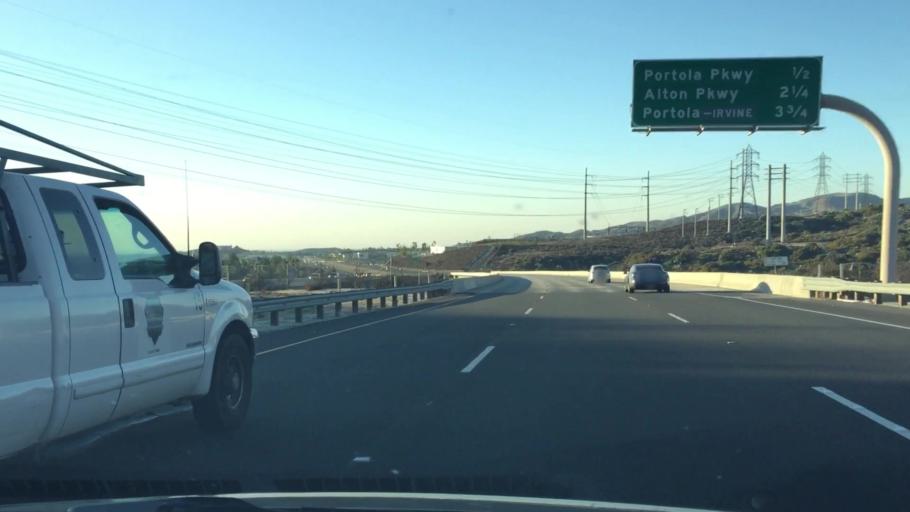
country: US
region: California
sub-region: Orange County
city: Portola Hills
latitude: 33.6618
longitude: -117.6366
